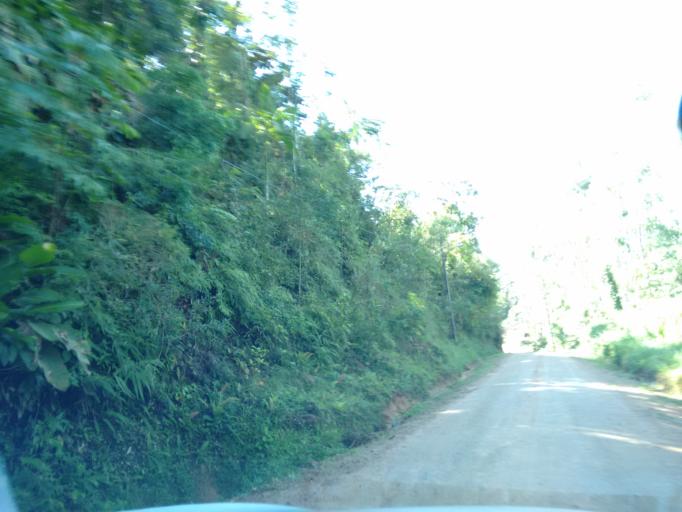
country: BR
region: Santa Catarina
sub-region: Pomerode
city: Pomerode
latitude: -26.7604
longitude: -49.1890
